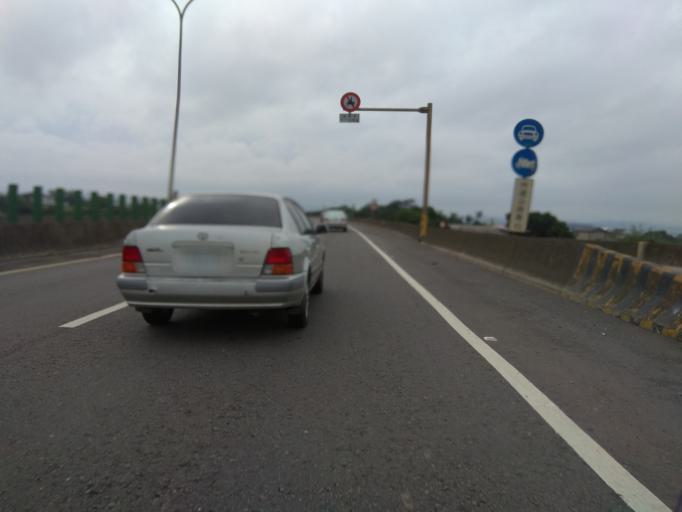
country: TW
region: Taiwan
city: Taoyuan City
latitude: 24.9642
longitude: 121.1344
